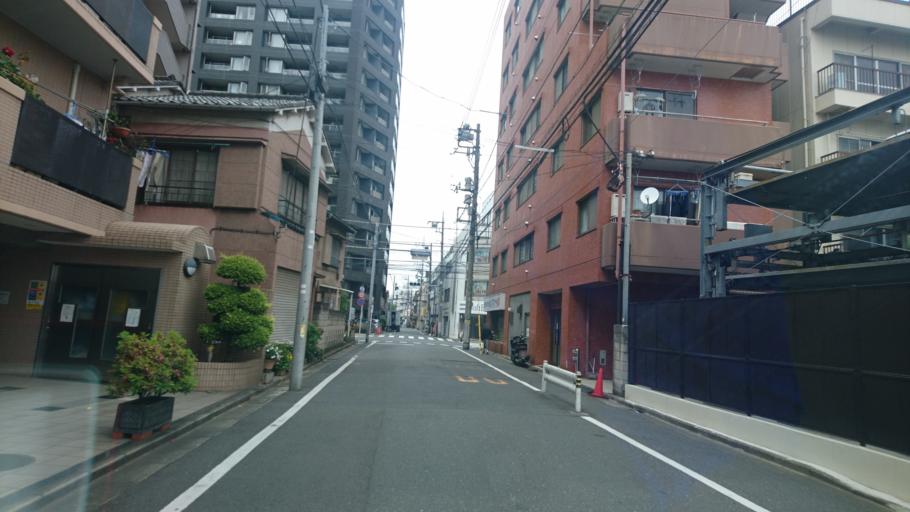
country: JP
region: Kanagawa
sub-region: Kawasaki-shi
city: Kawasaki
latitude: 35.5727
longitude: 139.7052
